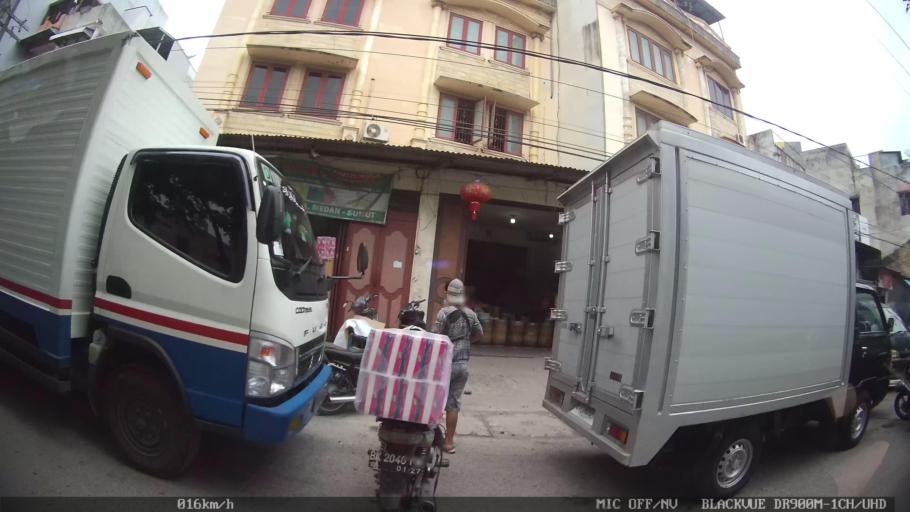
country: ID
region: North Sumatra
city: Medan
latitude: 3.5832
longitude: 98.7042
